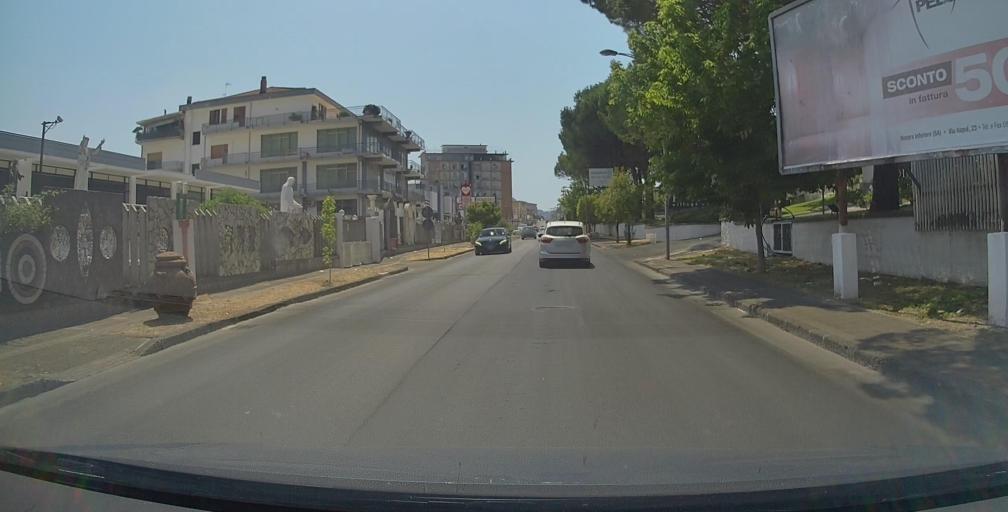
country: IT
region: Campania
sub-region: Provincia di Salerno
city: Nocera Superiore
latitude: 40.7314
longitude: 14.6875
